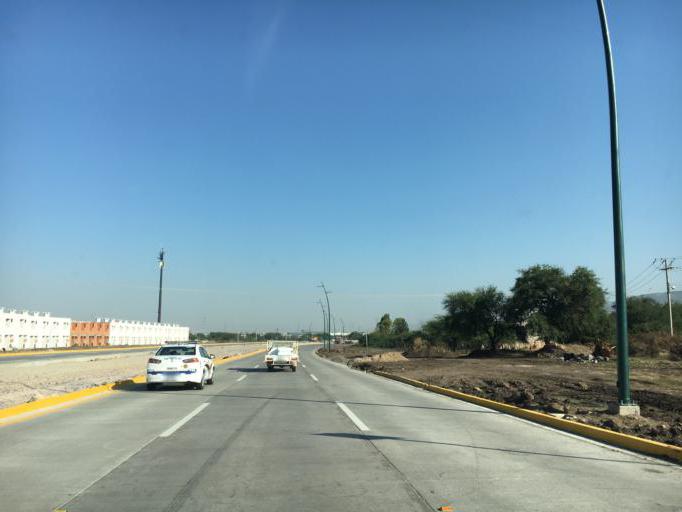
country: MX
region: Guanajuato
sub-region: Leon
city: Fraccionamiento Paraiso Real
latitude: 21.1123
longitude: -101.5872
